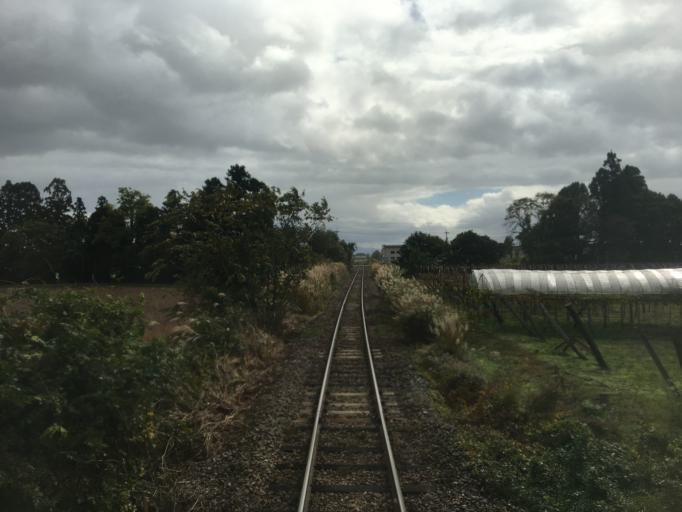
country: JP
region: Yamagata
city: Nagai
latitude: 38.0644
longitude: 140.0363
